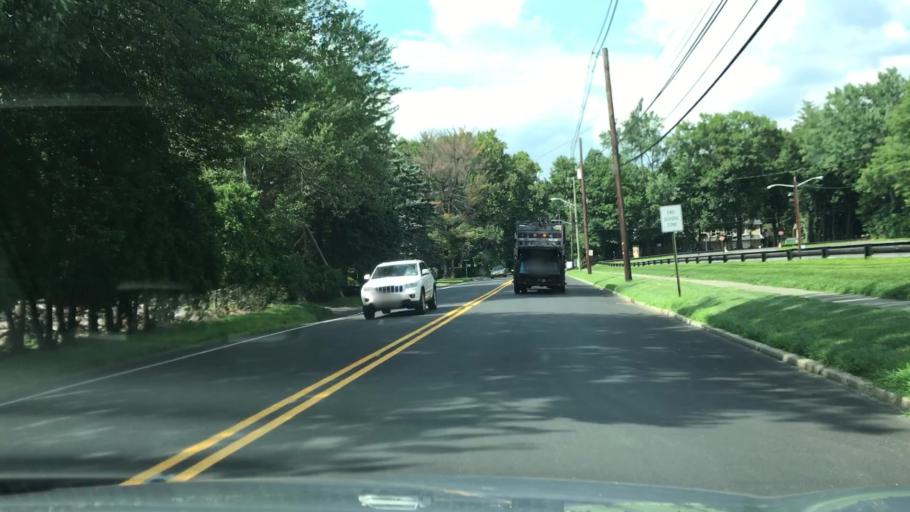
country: US
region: New Jersey
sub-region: Bergen County
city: Demarest
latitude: 40.9648
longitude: -73.9743
